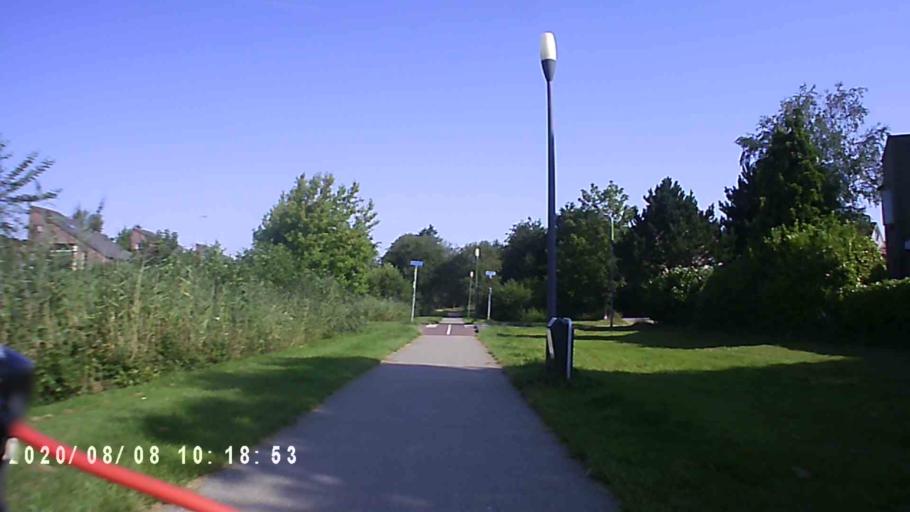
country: NL
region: Groningen
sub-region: Gemeente Leek
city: Leek
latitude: 53.1349
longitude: 6.4012
